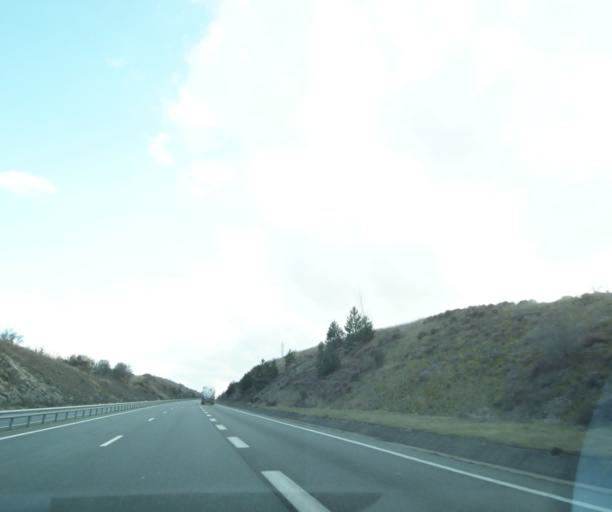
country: FR
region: Midi-Pyrenees
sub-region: Departement du Lot
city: Le Vigan
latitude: 44.7170
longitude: 1.5668
